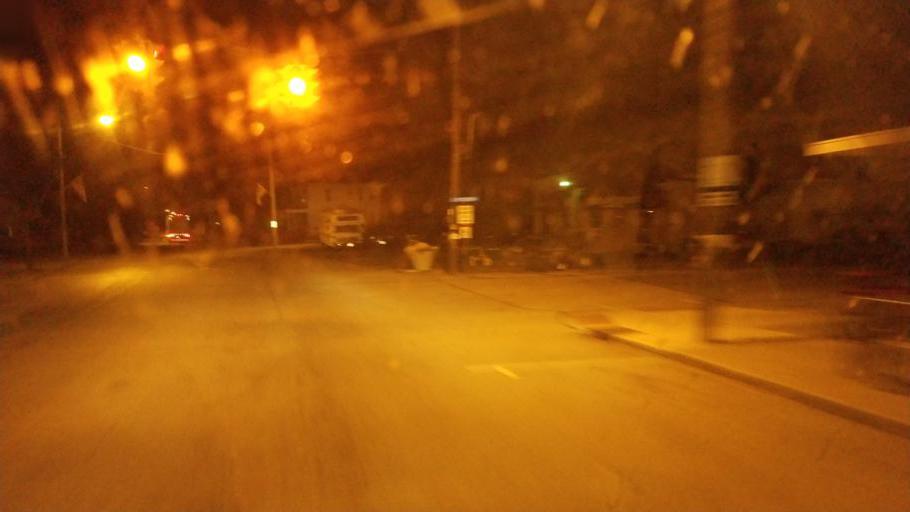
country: US
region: Ohio
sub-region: Hancock County
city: Arlington
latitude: 40.7901
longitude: -83.6435
